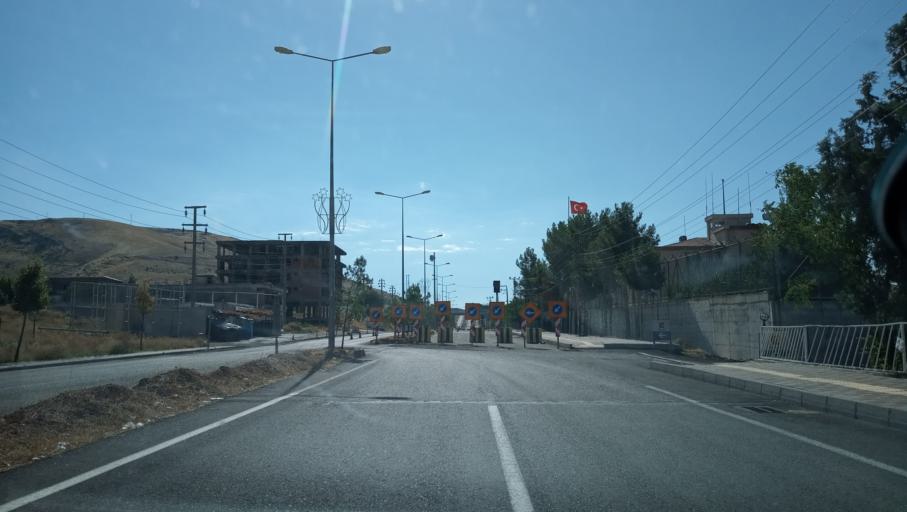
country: TR
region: Diyarbakir
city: Silvan
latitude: 38.1353
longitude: 41.0296
